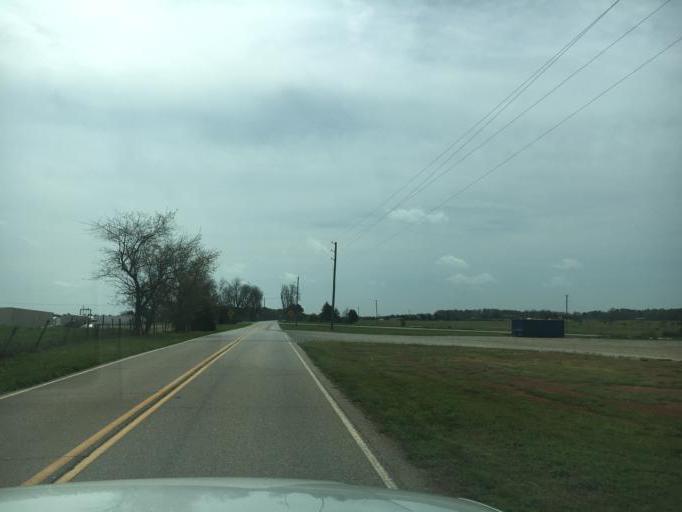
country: US
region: Georgia
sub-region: Hart County
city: Royston
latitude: 34.3041
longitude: -83.0454
